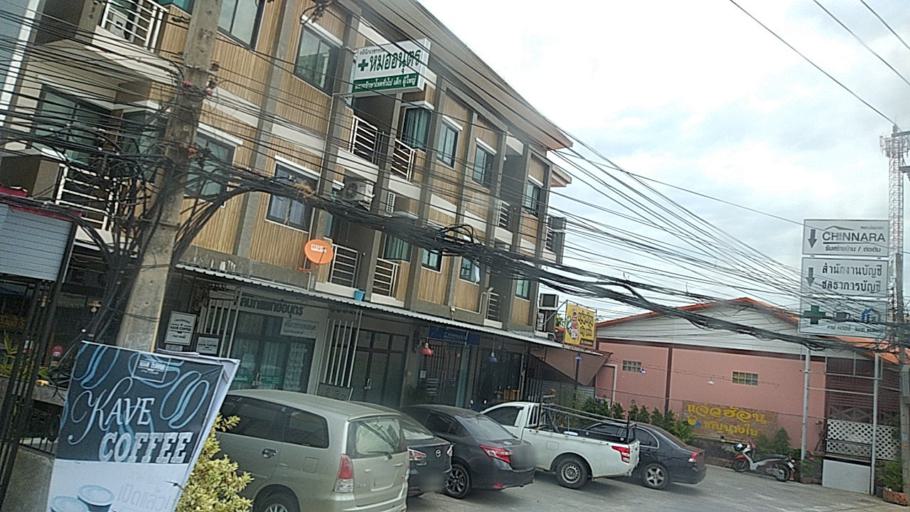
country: TH
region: Maha Sarakham
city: Maha Sarakham
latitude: 16.1733
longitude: 103.3179
